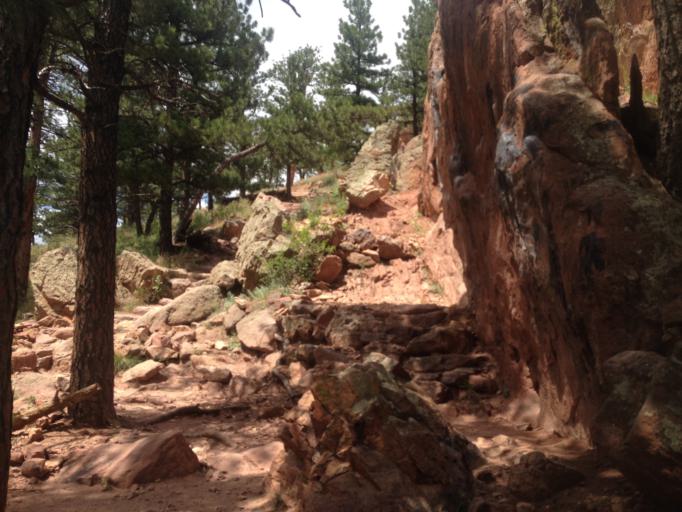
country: US
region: Colorado
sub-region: Boulder County
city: Boulder
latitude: 40.0225
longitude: -105.2984
